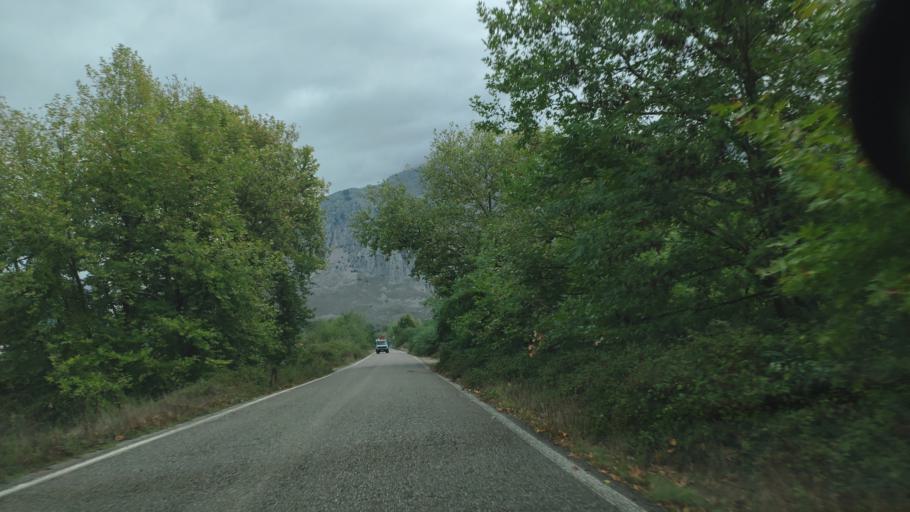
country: GR
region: West Greece
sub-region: Nomos Aitolias kai Akarnanias
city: Krikellos
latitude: 38.9655
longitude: 21.3284
